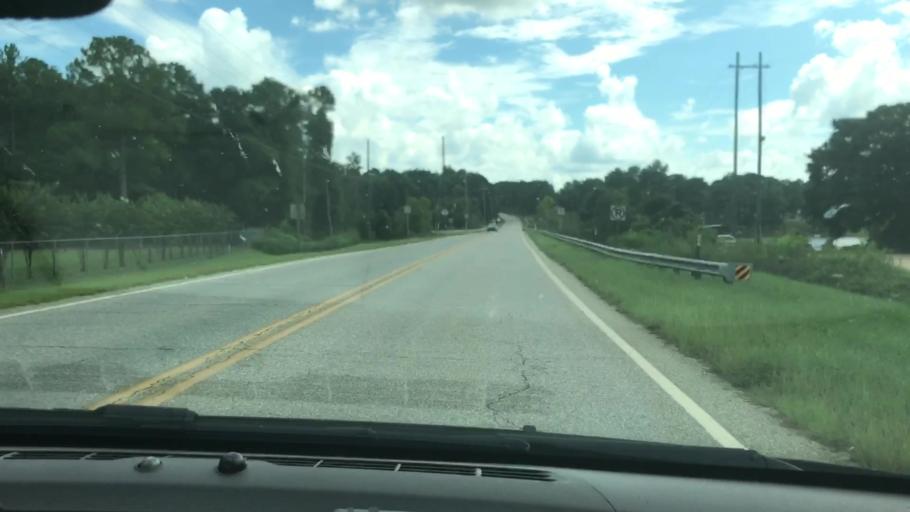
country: US
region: Georgia
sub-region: Clay County
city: Fort Gaines
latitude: 31.7493
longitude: -85.0549
